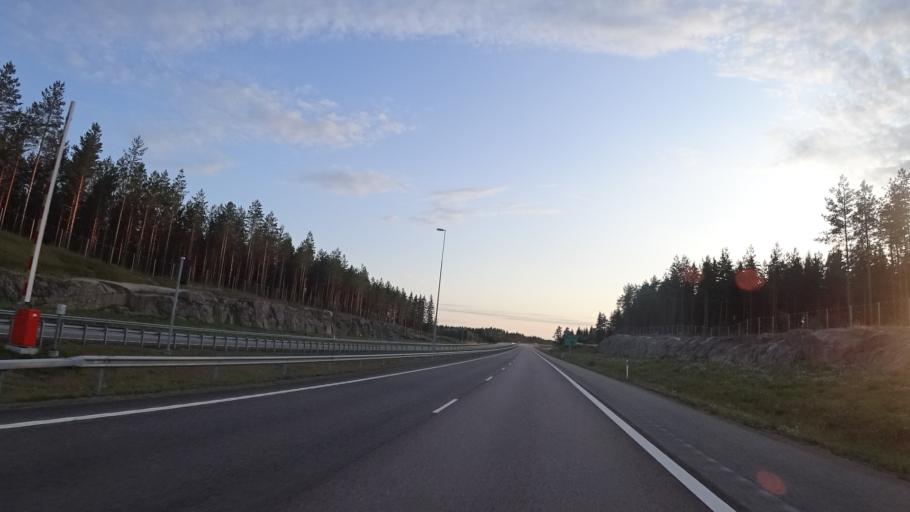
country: FI
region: Kymenlaakso
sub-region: Kotka-Hamina
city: Virojoki
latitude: 60.6116
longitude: 27.7831
